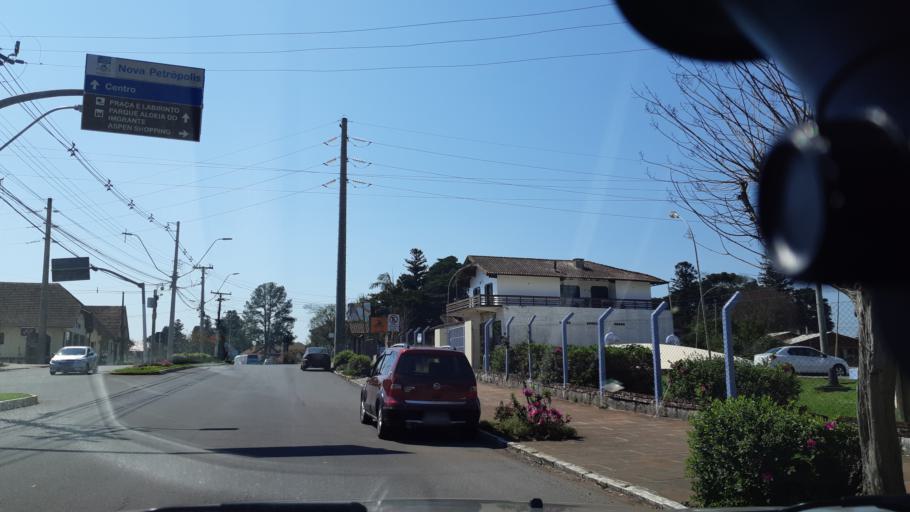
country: BR
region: Rio Grande do Sul
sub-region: Nova Petropolis
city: Nova Petropolis
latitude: -29.3830
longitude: -51.1176
